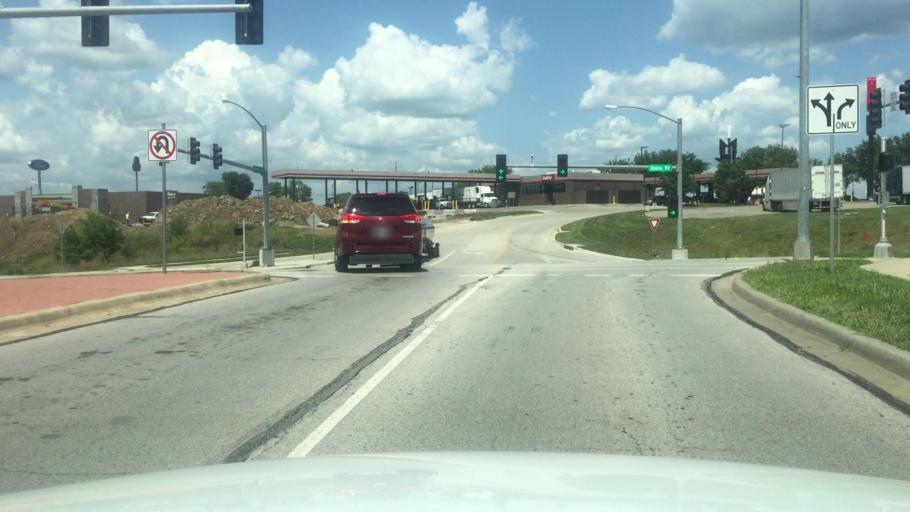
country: US
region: Missouri
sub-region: Platte County
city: Platte City
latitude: 39.3536
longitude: -94.7671
